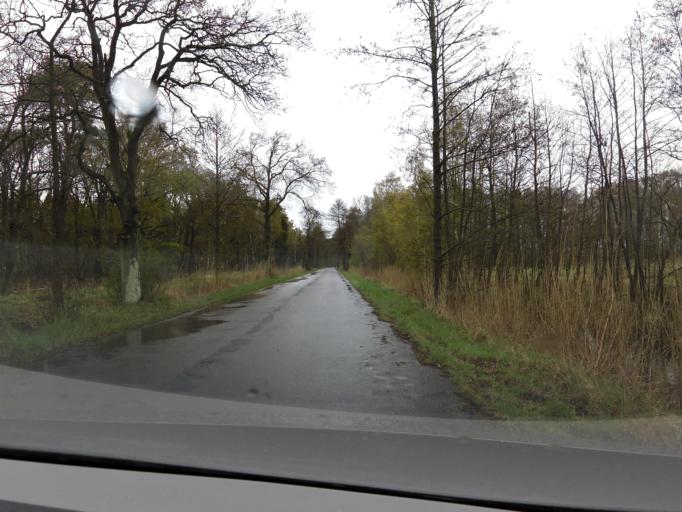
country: DE
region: Mecklenburg-Vorpommern
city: Barth
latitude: 54.4259
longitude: 12.7983
